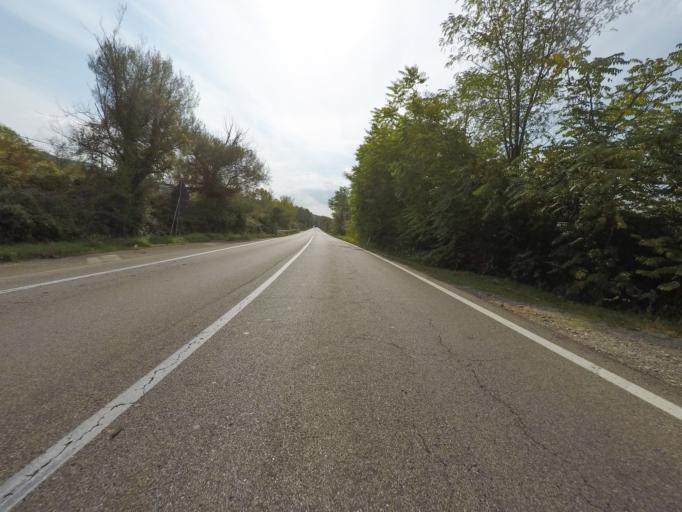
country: IT
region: Tuscany
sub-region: Provincia di Siena
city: Rosia
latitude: 43.1998
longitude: 11.2760
